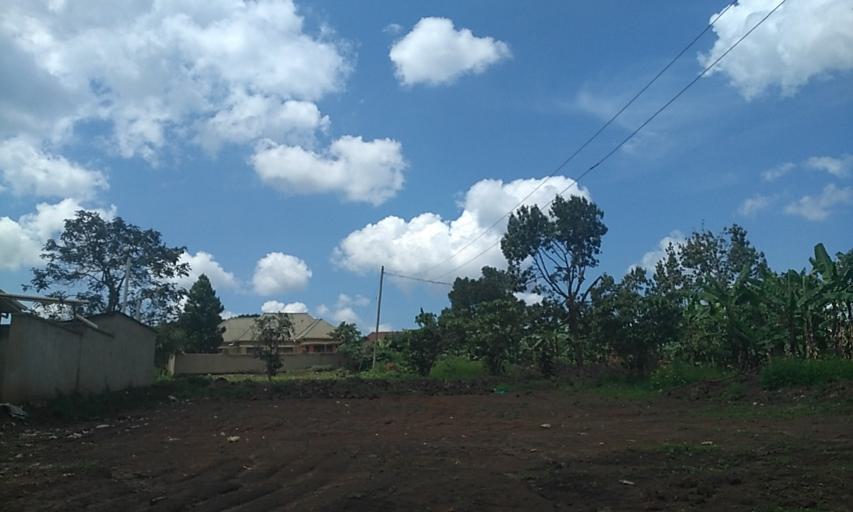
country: UG
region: Central Region
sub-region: Wakiso District
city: Wakiso
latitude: 0.3912
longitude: 32.4635
